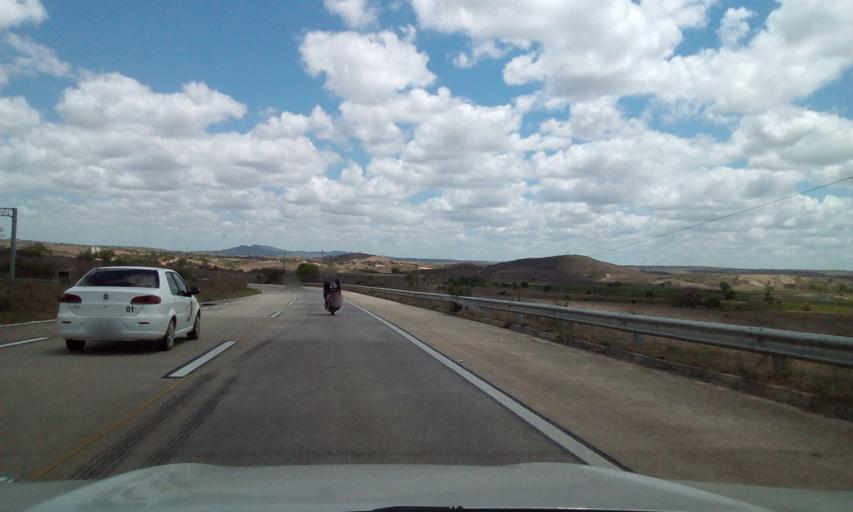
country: BR
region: Alagoas
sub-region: Porto Real Do Colegio
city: Porto Real do Colegio
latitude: -10.1613
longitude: -36.8138
